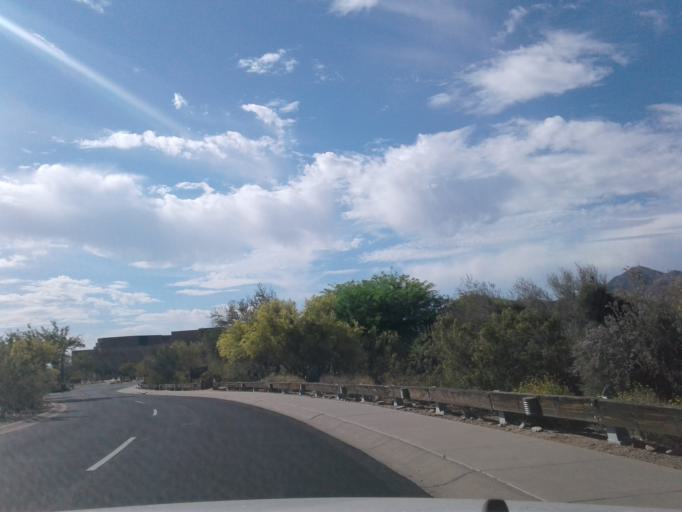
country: US
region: Arizona
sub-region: Maricopa County
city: Fountain Hills
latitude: 33.5845
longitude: -111.7916
